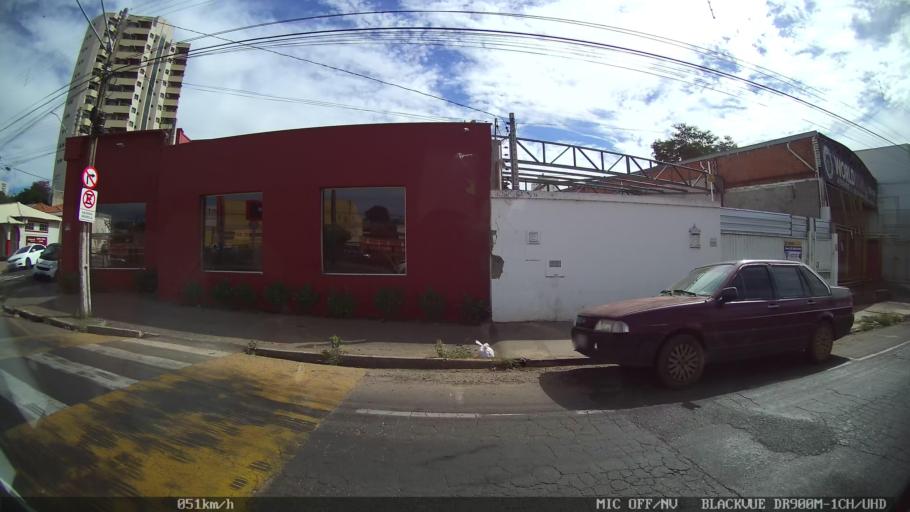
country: BR
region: Sao Paulo
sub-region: Catanduva
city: Catanduva
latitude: -21.1427
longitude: -48.9705
